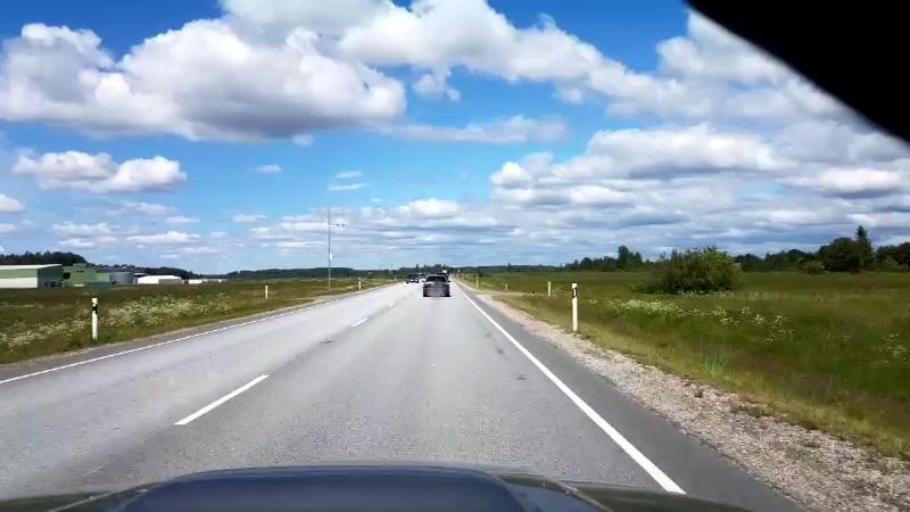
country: EE
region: Paernumaa
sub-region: Sauga vald
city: Sauga
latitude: 58.4832
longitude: 24.5279
